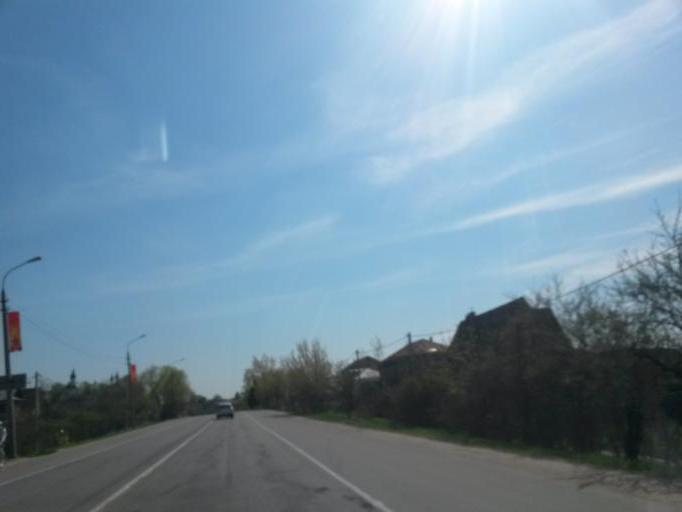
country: RU
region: Moskovskaya
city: Stolbovaya
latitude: 55.2783
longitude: 37.5100
